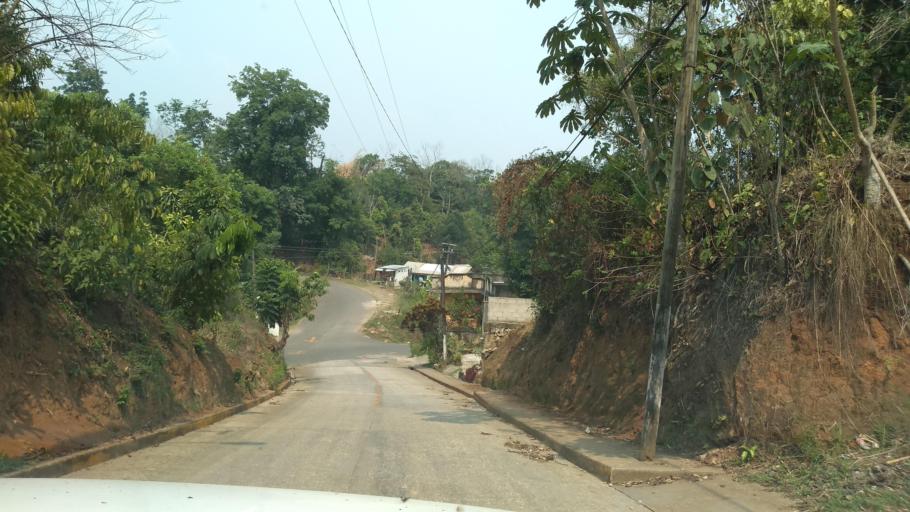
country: MX
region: Veracruz
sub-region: Tezonapa
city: Laguna Chica (Pueblo Nuevo)
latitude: 18.5310
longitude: -96.7895
